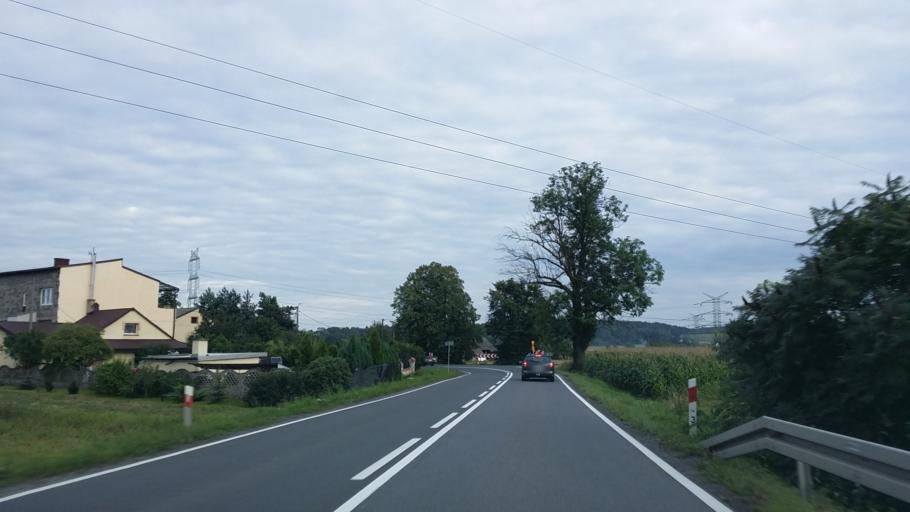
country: PL
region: Lesser Poland Voivodeship
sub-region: Powiat oswiecimski
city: Zator
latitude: 49.9952
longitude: 19.4572
